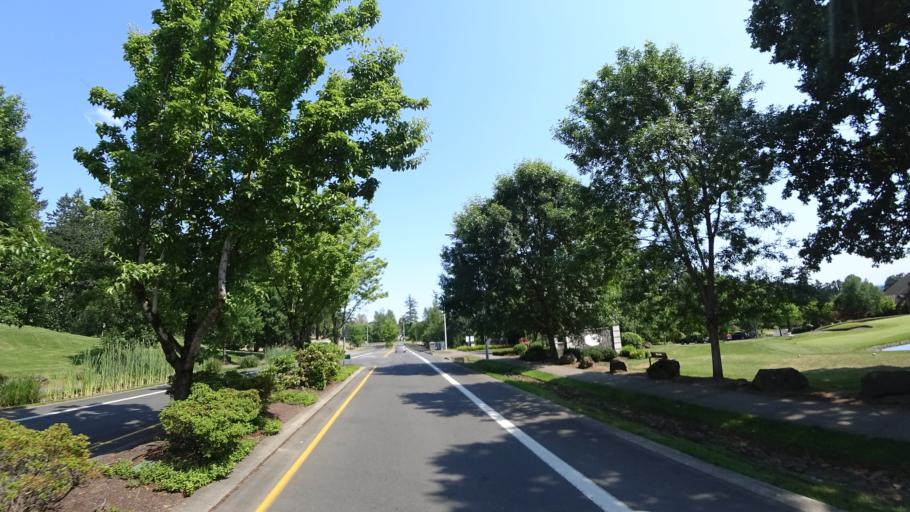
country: US
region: Oregon
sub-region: Clackamas County
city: Happy Valley
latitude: 45.4411
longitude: -122.5574
